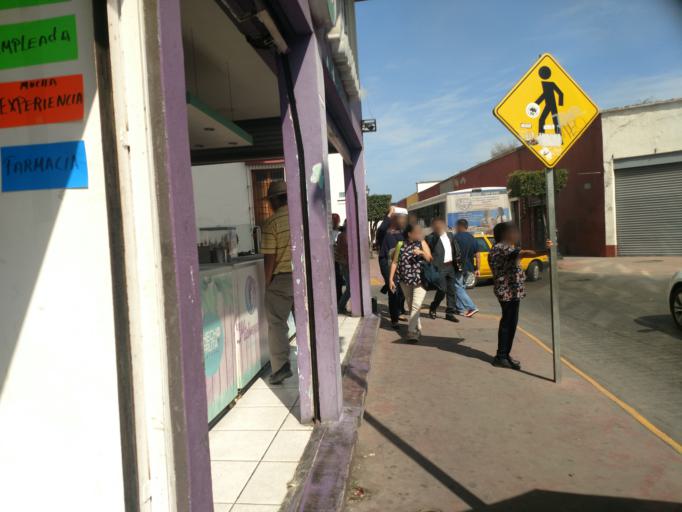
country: MX
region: Nayarit
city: Tepic
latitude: 21.5110
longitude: -104.8912
